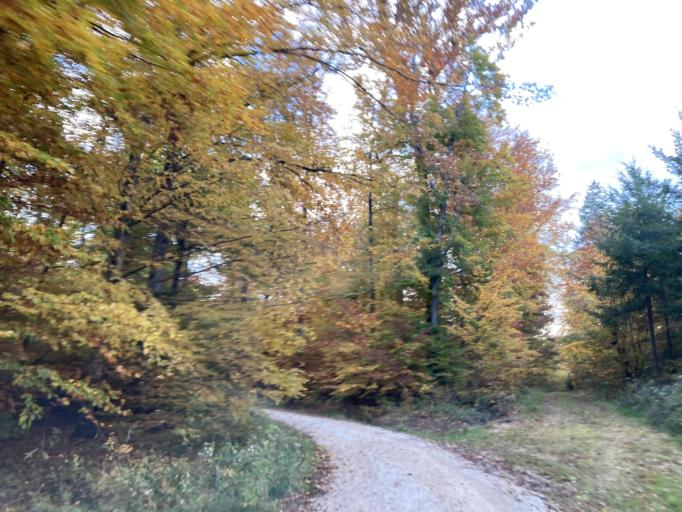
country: DE
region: Baden-Wuerttemberg
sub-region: Tuebingen Region
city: Gomaringen
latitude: 48.4623
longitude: 9.1313
